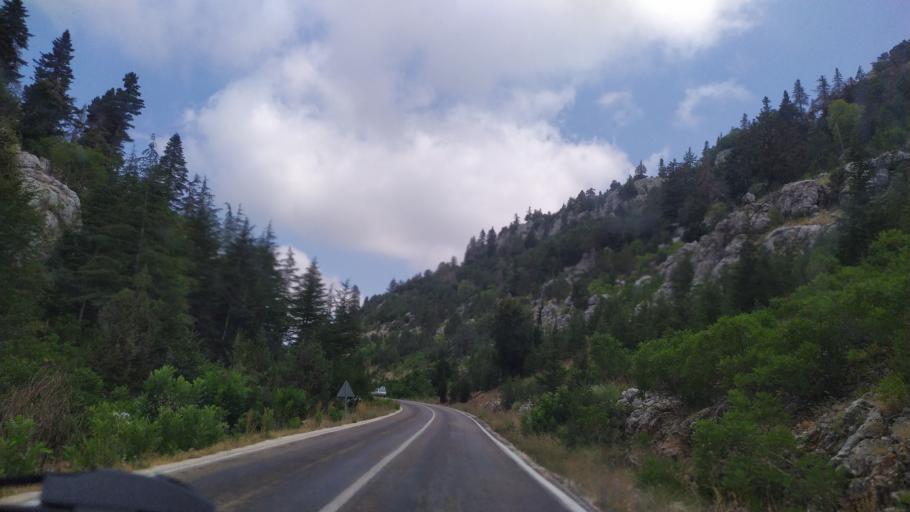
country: TR
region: Mersin
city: Kirobasi
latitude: 36.6073
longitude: 33.8837
